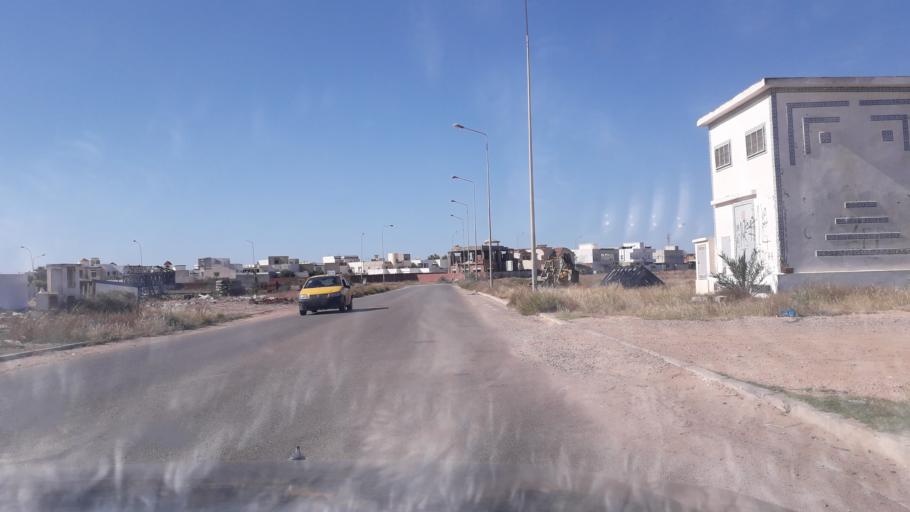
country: TN
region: Safaqis
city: Al Qarmadah
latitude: 34.8295
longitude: 10.7536
